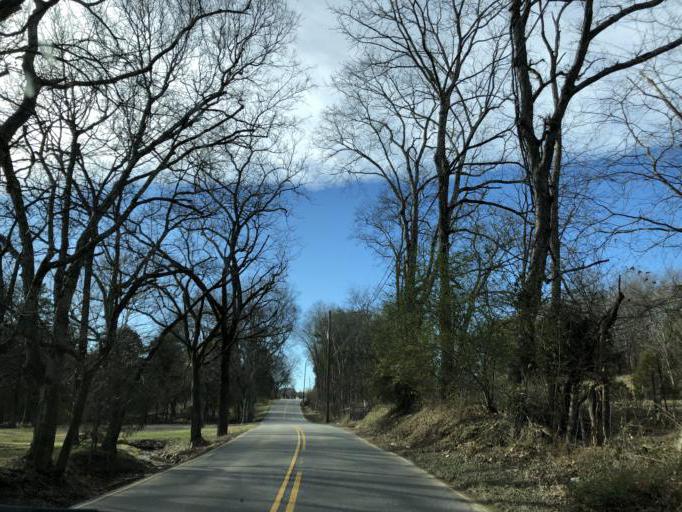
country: US
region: Tennessee
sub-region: Wilson County
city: Mount Juliet
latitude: 36.1593
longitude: -86.5658
